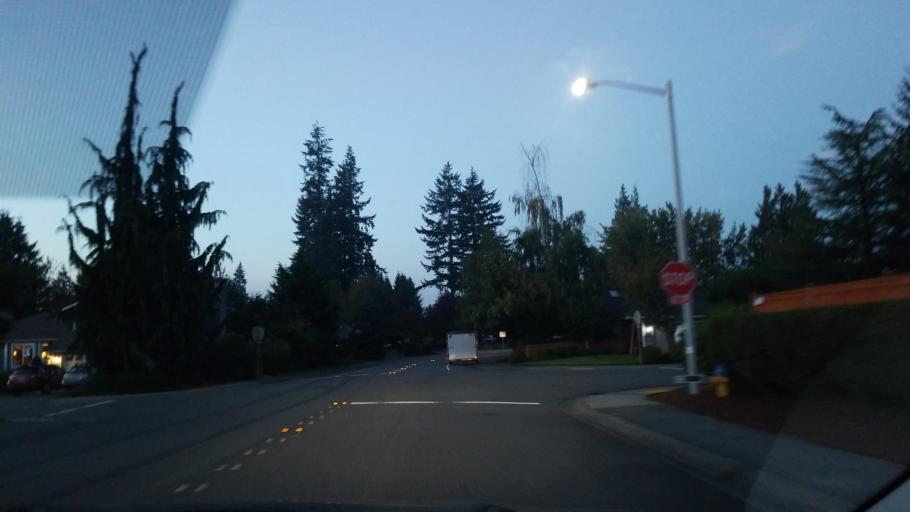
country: US
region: Washington
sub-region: Snohomish County
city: Silver Firs
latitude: 47.8825
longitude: -122.1718
